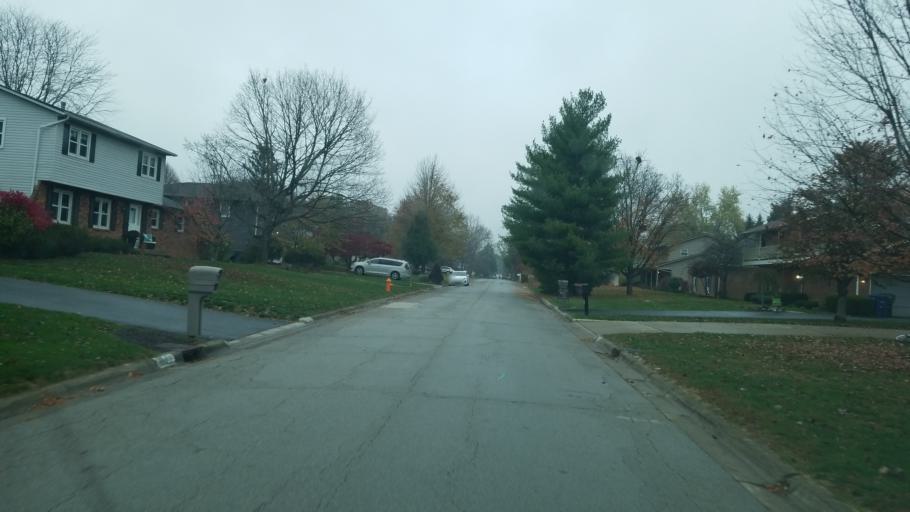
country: US
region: Ohio
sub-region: Franklin County
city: Worthington
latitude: 40.0792
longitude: -83.0470
